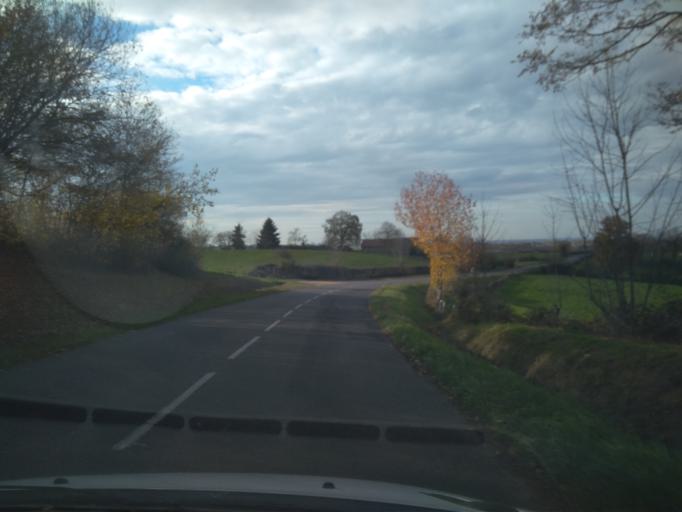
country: FR
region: Auvergne
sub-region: Departement de l'Allier
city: Le Mayet-de-Montagne
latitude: 46.1672
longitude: 3.6939
